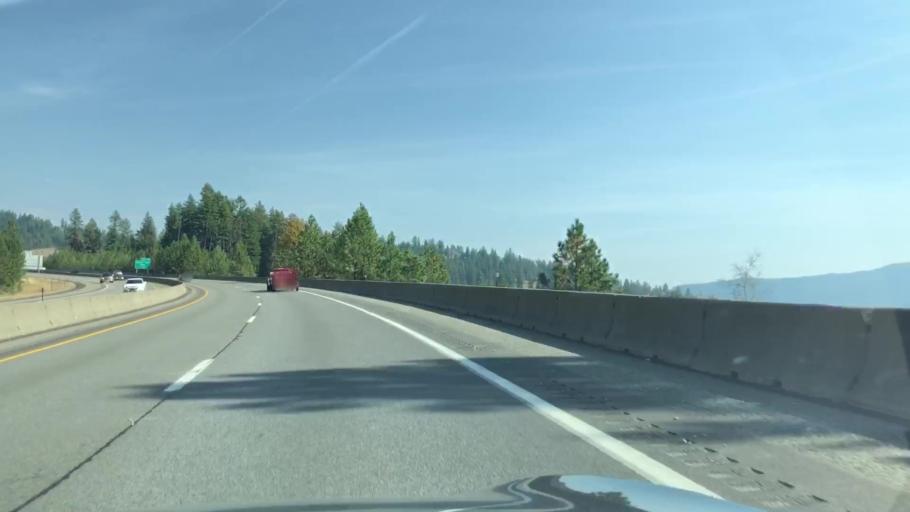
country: US
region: Idaho
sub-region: Kootenai County
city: Coeur d'Alene
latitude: 47.6628
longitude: -116.7475
